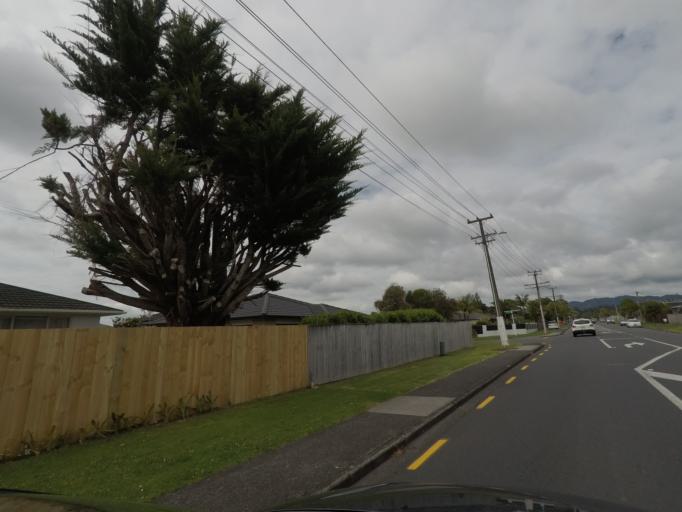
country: NZ
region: Auckland
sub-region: Auckland
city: Waitakere
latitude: -36.8969
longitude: 174.6261
